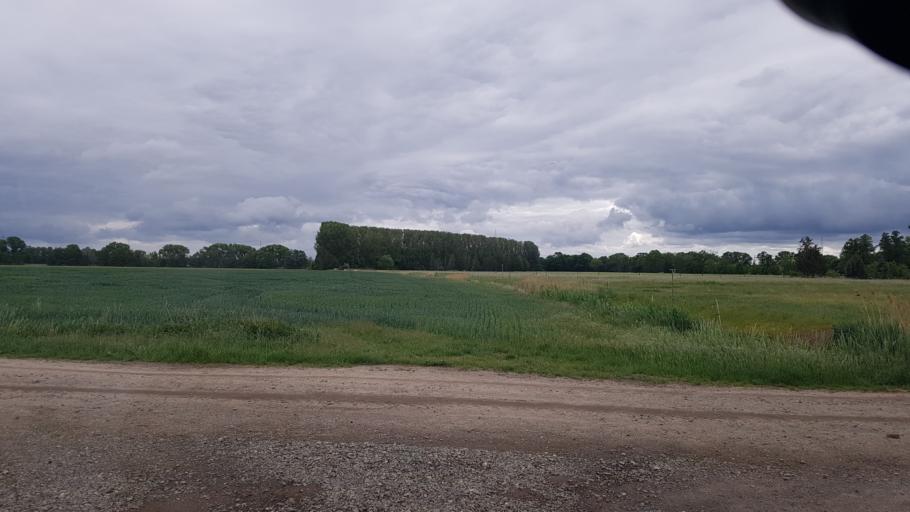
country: DE
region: Brandenburg
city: Doberlug-Kirchhain
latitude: 51.6530
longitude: 13.5504
